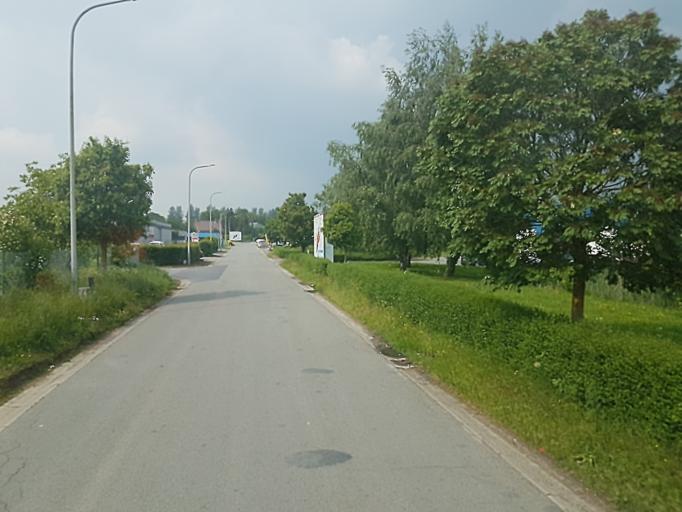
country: BE
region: Flanders
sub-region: Provincie Oost-Vlaanderen
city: Geraardsbergen
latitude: 50.7919
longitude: 3.8767
